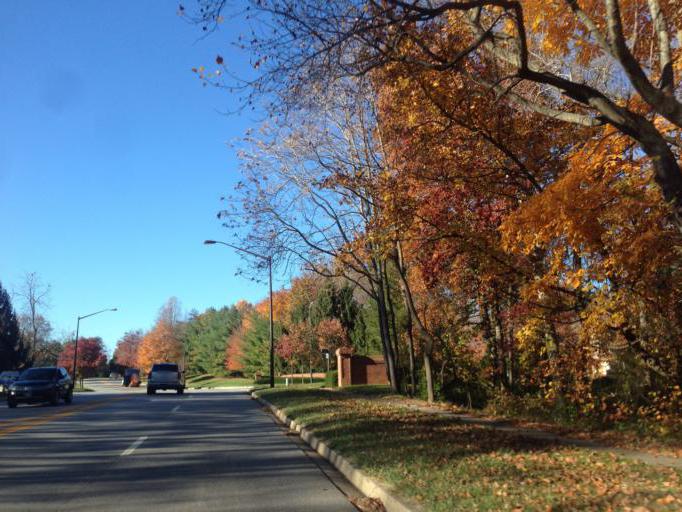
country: US
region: Maryland
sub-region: Howard County
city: Columbia
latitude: 39.2310
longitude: -76.8969
